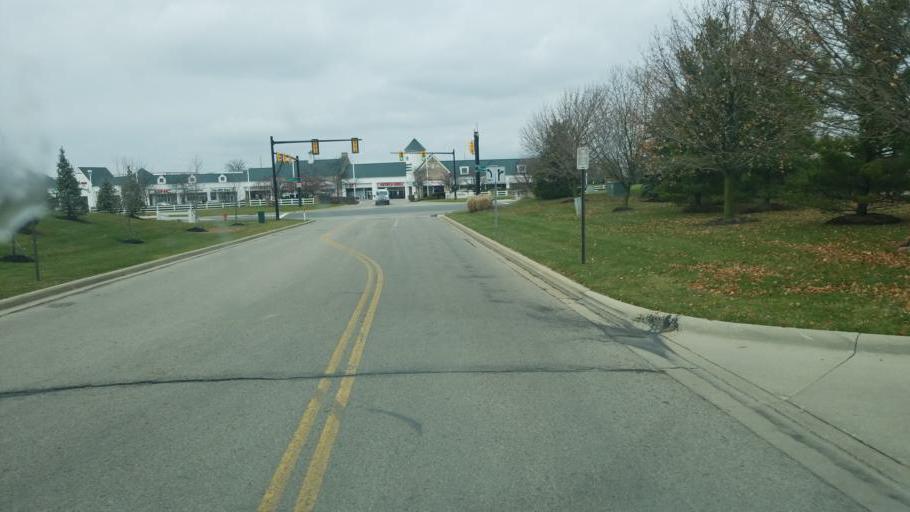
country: US
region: Ohio
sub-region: Delaware County
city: Powell
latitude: 40.1604
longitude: -83.0901
